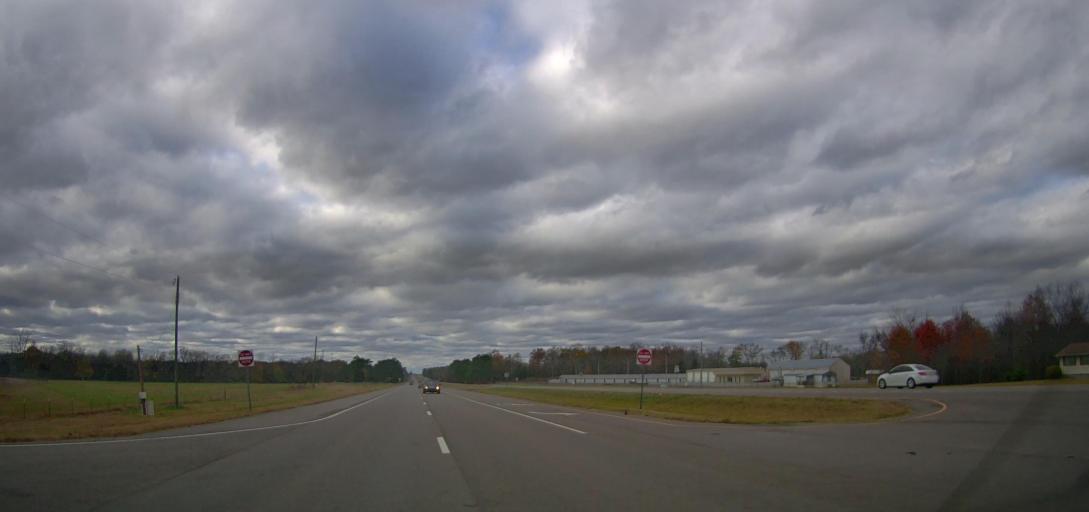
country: US
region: Alabama
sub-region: Morgan County
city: Danville
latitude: 34.3438
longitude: -87.0323
